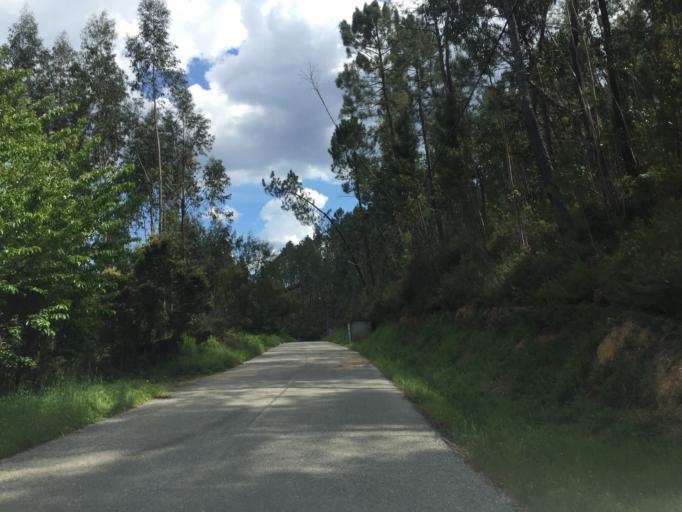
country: PT
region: Coimbra
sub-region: Pampilhosa da Serra
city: Pampilhosa da Serra
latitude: 40.0495
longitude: -7.8116
